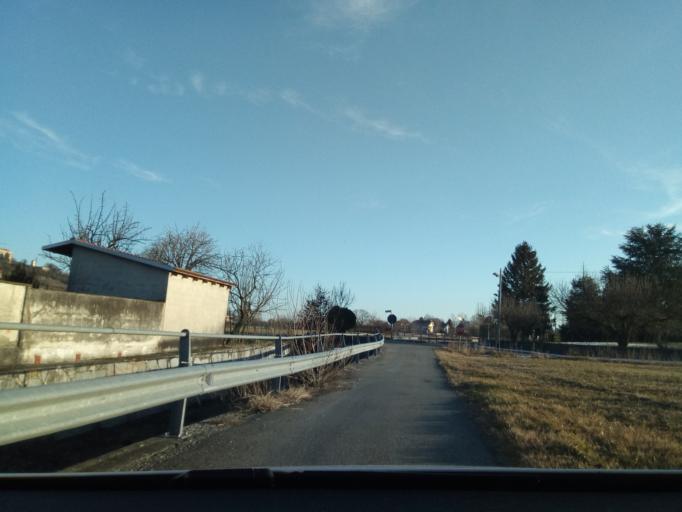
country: IT
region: Piedmont
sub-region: Provincia di Torino
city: Burolo
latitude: 45.4776
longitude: 7.9276
